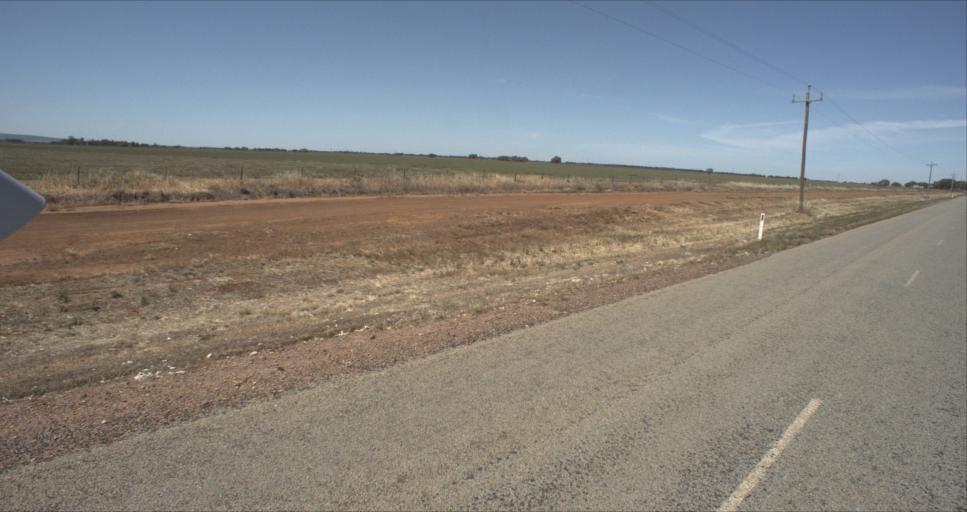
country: AU
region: New South Wales
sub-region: Leeton
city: Leeton
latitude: -34.4522
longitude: 146.2958
